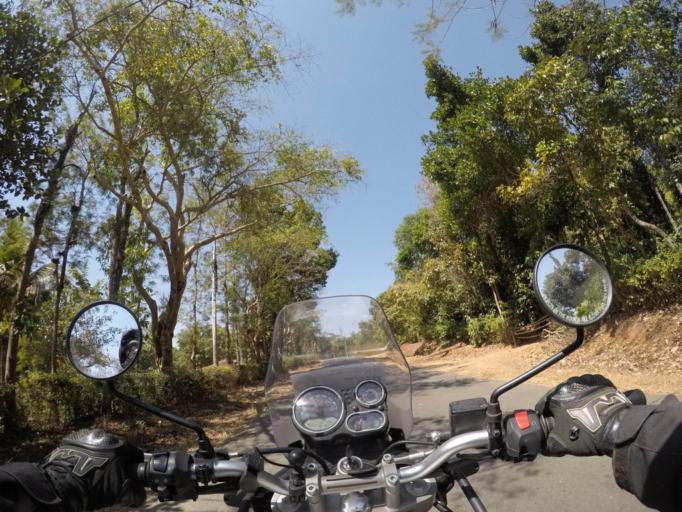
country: IN
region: Karnataka
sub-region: Chikmagalur
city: Mudigere
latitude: 13.0754
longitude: 75.6828
